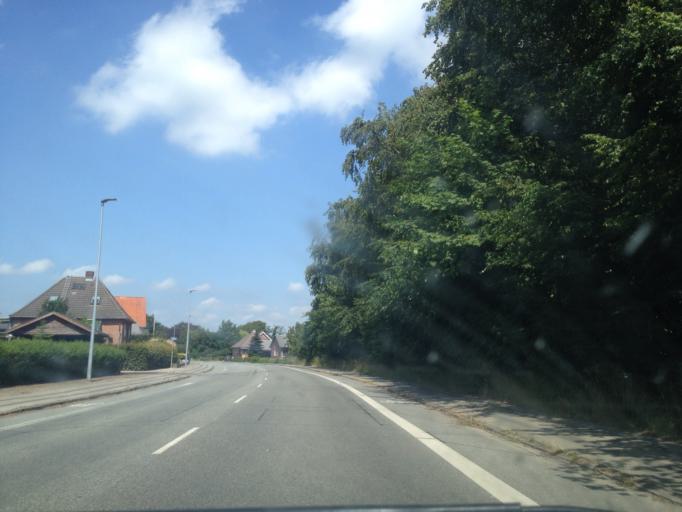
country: DK
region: South Denmark
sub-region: Kolding Kommune
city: Vamdrup
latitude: 55.4297
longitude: 9.2877
